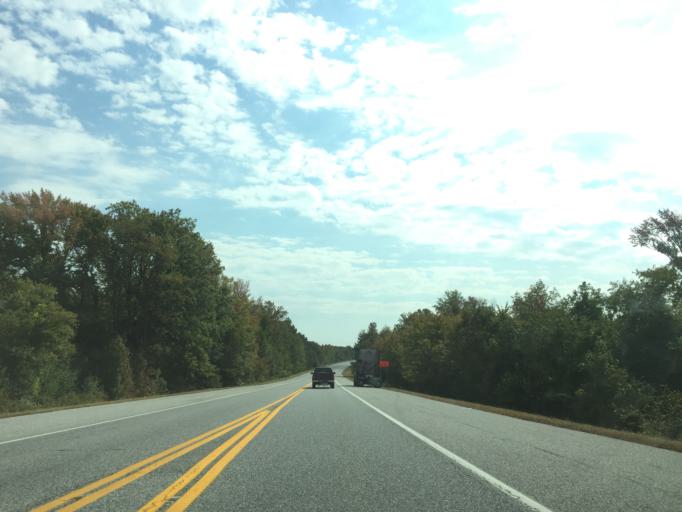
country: US
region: Maryland
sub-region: Harford County
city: Edgewood
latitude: 39.4164
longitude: -76.3067
